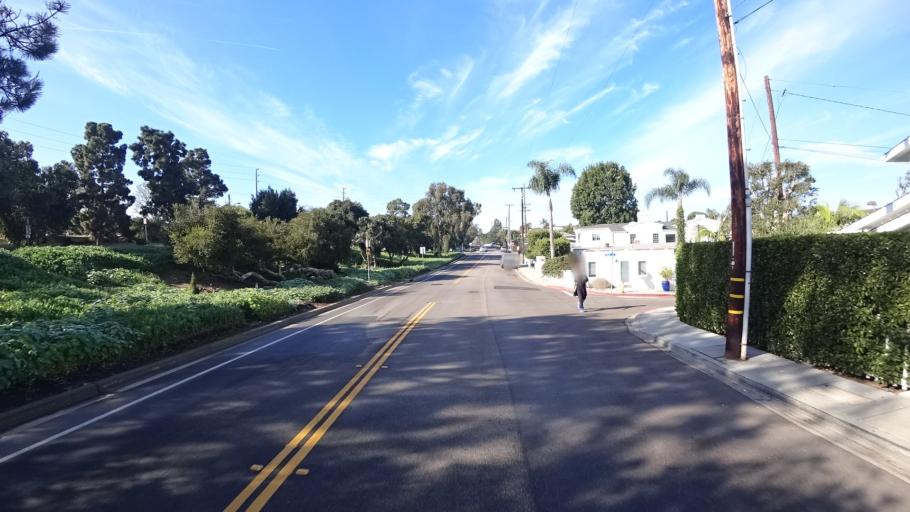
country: US
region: California
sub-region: Los Angeles County
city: Manhattan Beach
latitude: 33.8952
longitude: -118.4023
